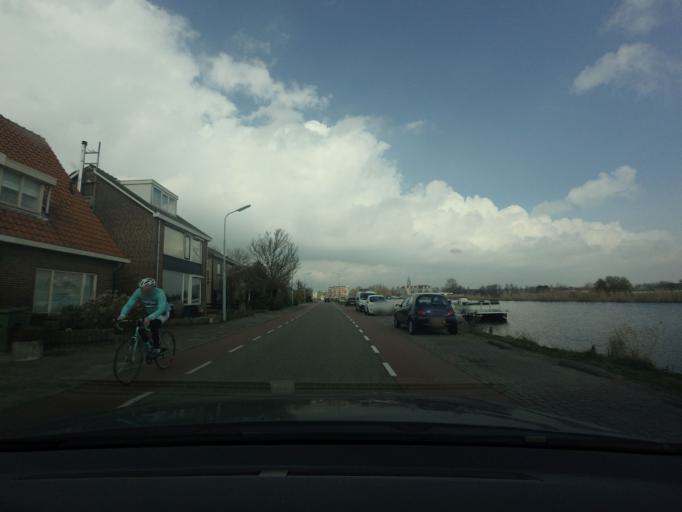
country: NL
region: North Holland
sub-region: Gemeente Zaanstad
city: Zaandam
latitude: 52.3768
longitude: 4.7567
